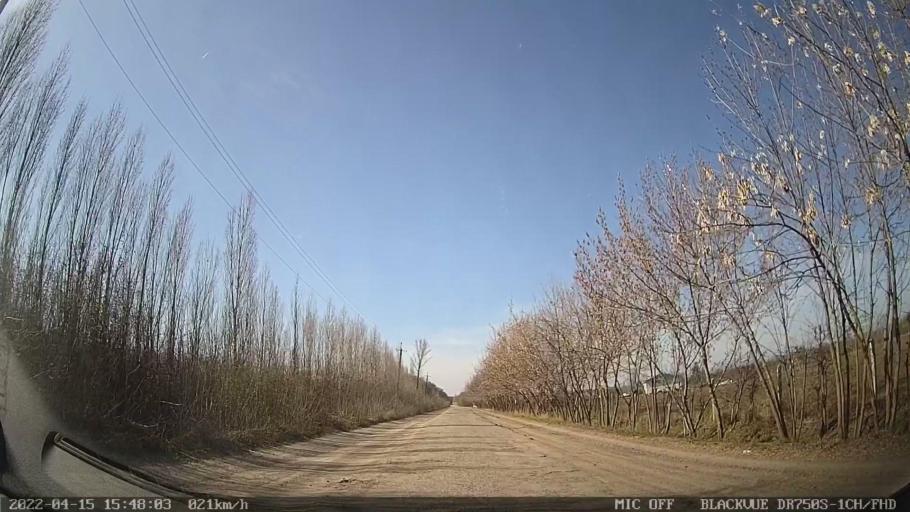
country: MD
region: Raionul Ocnita
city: Otaci
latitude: 48.3859
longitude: 27.9081
